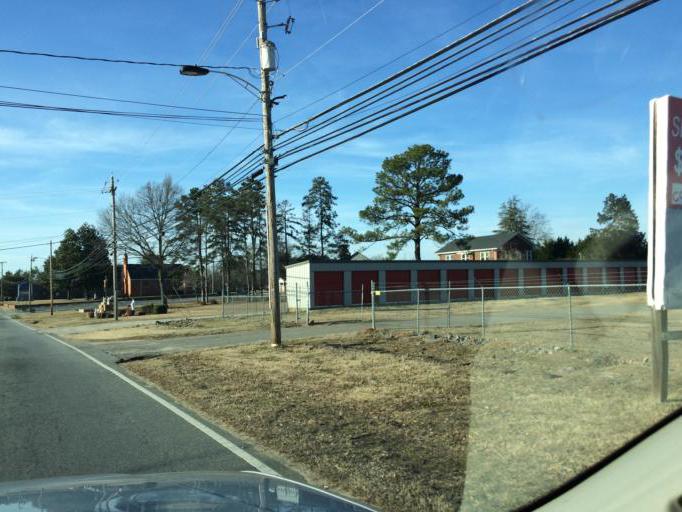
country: US
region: North Carolina
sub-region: Rutherford County
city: Forest City
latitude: 35.3482
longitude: -81.8874
